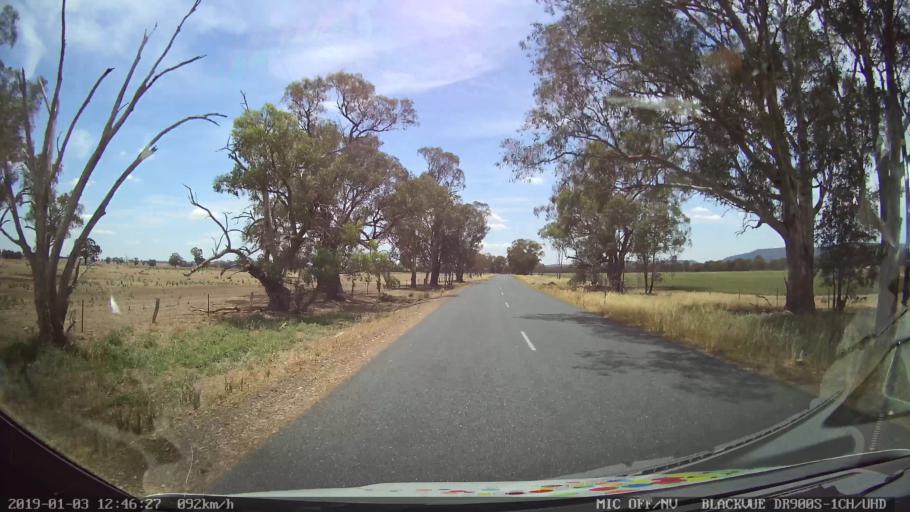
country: AU
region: New South Wales
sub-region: Weddin
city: Grenfell
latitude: -33.7382
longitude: 148.2335
